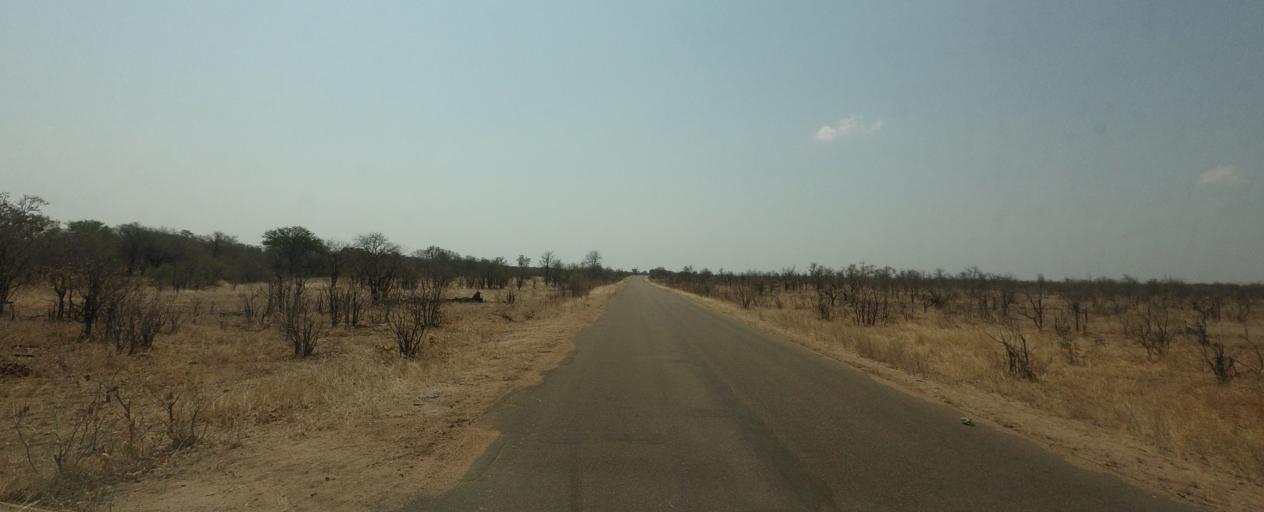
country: ZA
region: Limpopo
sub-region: Mopani District Municipality
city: Phalaborwa
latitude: -23.3797
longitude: 31.3245
